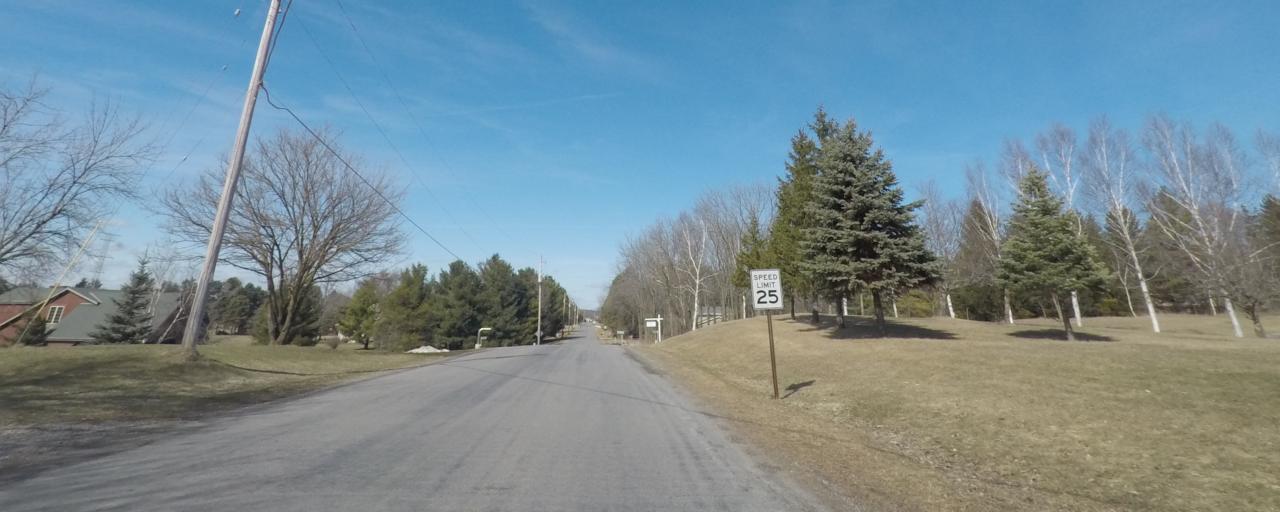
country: US
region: Wisconsin
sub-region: Waukesha County
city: Merton
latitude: 43.1561
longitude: -88.3215
